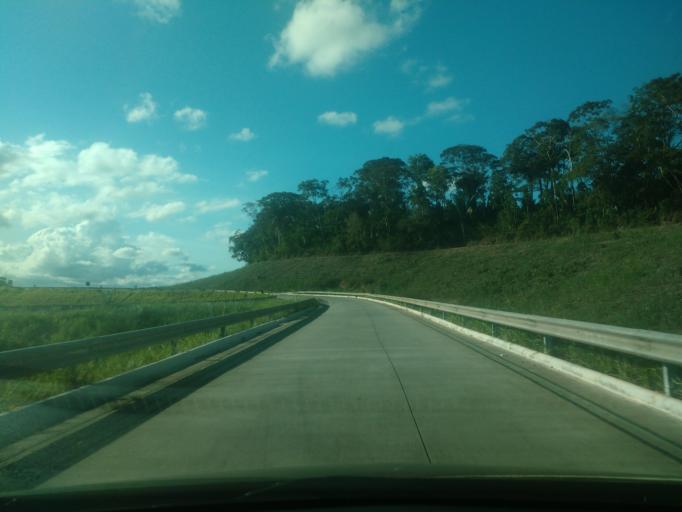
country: BR
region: Alagoas
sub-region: Messias
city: Messias
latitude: -9.3694
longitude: -35.8306
